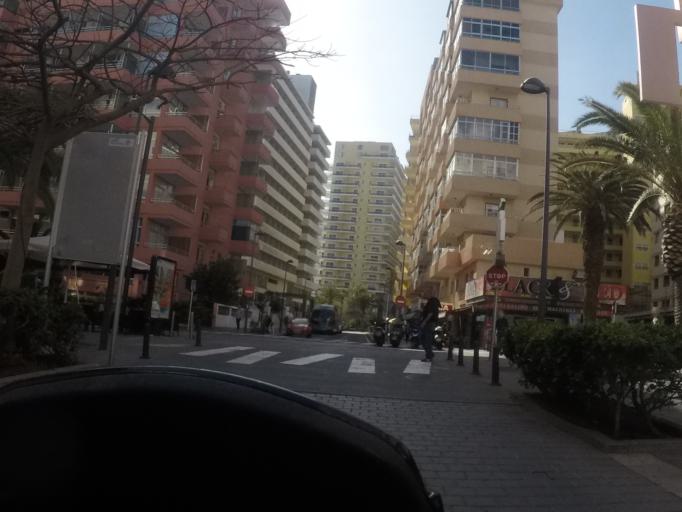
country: ES
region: Canary Islands
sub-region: Provincia de Santa Cruz de Tenerife
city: Puerto de la Cruz
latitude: 28.4177
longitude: -16.5433
